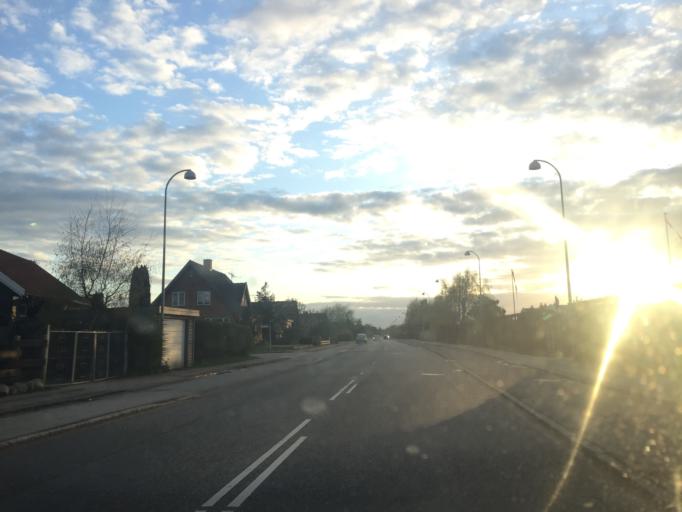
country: DK
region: Capital Region
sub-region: Hvidovre Kommune
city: Hvidovre
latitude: 55.6451
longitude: 12.4591
